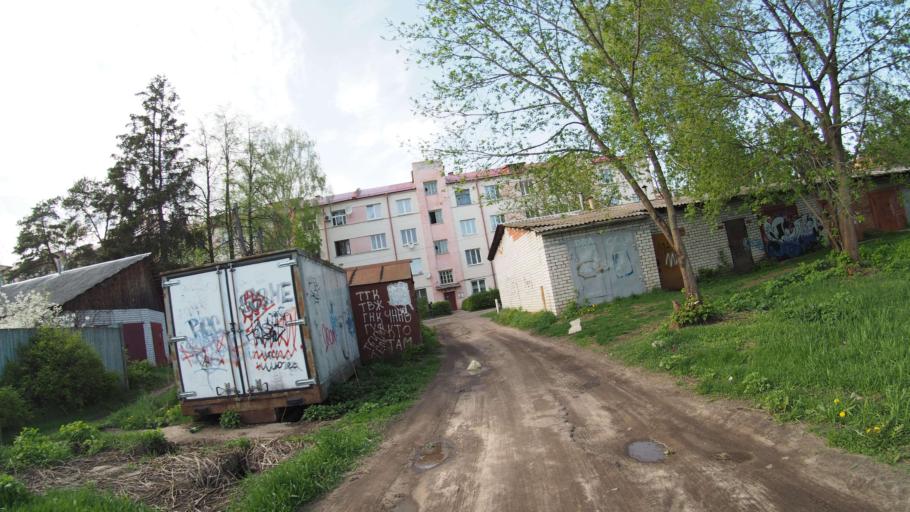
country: RU
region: Moskovskaya
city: Ramenskoye
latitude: 55.5695
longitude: 38.2025
